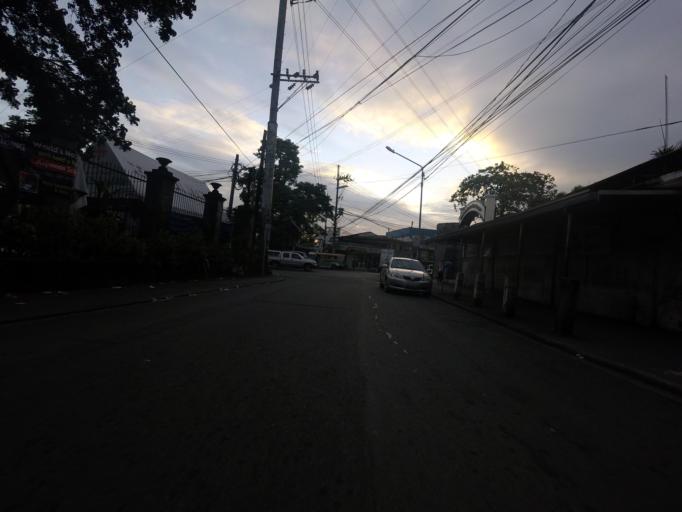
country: PH
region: Metro Manila
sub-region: San Juan
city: San Juan
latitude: 14.5984
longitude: 121.0302
